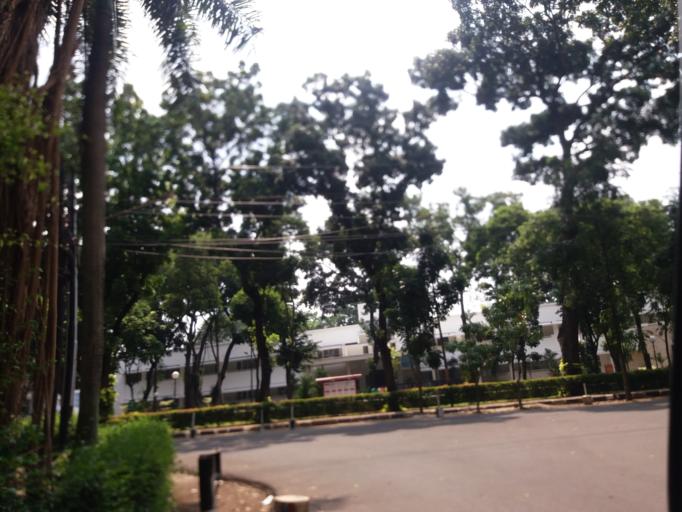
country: ID
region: Jakarta Raya
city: Jakarta
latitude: -6.2331
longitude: 106.8017
